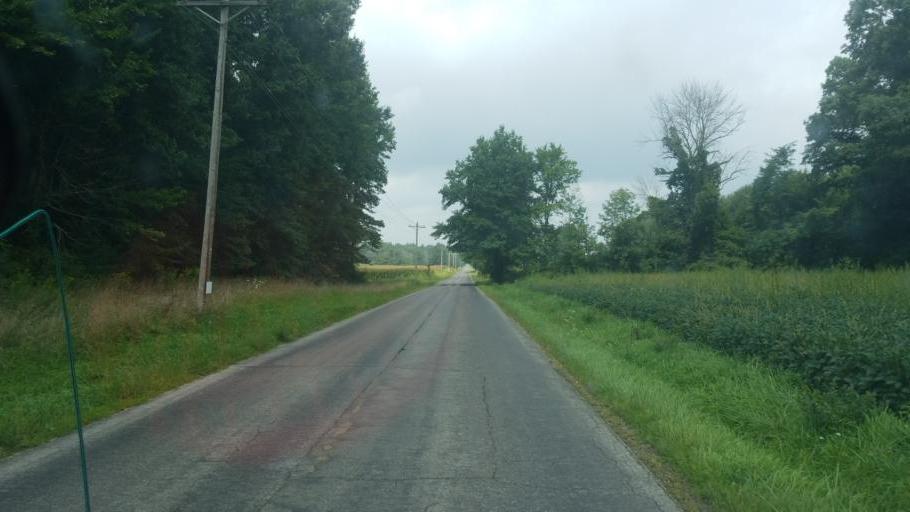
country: US
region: Ohio
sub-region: Huron County
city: Greenwich
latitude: 40.9823
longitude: -82.4742
